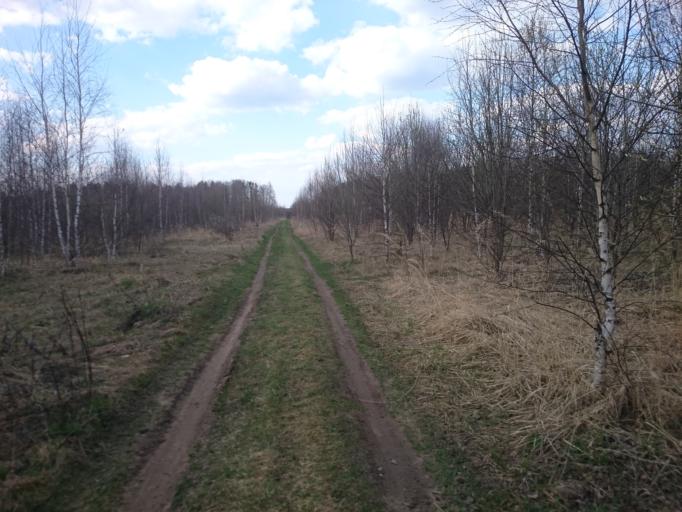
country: RU
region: Moskovskaya
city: Klin
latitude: 56.4011
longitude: 36.6811
